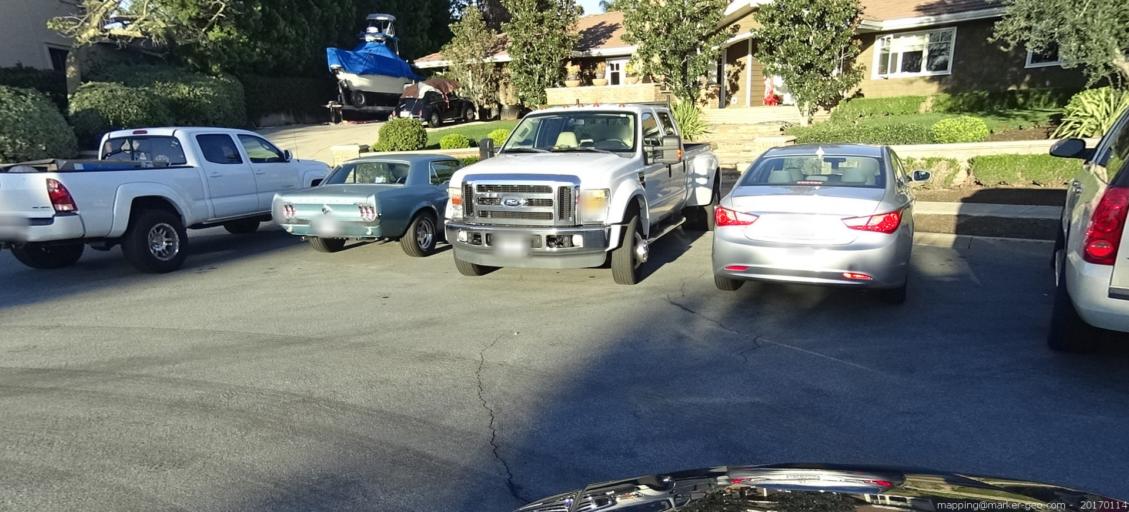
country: US
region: California
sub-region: Orange County
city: Tustin
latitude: 33.7639
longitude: -117.8161
